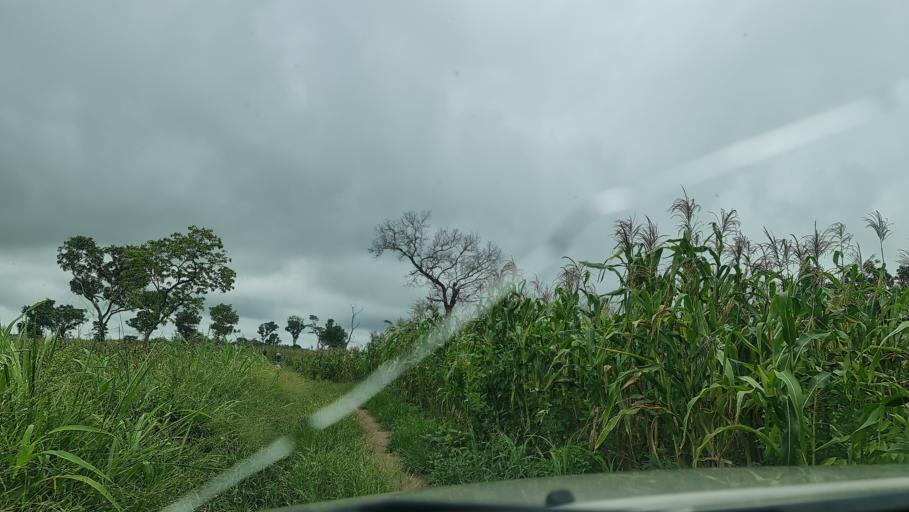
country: MW
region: Southern Region
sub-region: Nsanje District
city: Nsanje
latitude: -17.3403
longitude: 35.7296
